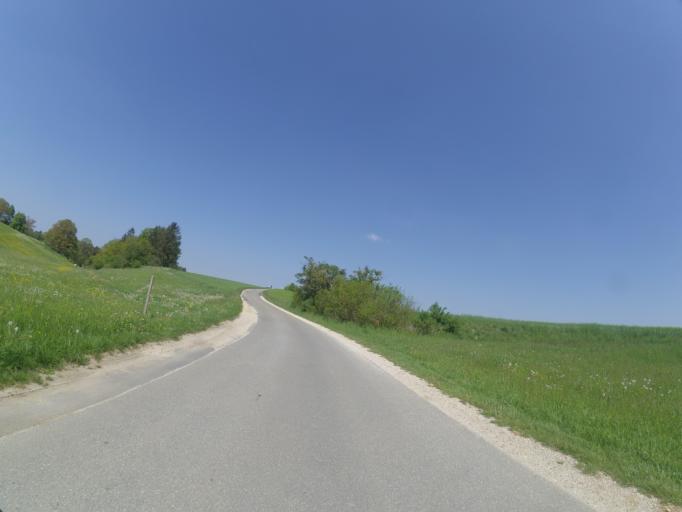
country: DE
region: Baden-Wuerttemberg
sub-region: Tuebingen Region
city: Berghulen
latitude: 48.4762
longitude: 9.8245
